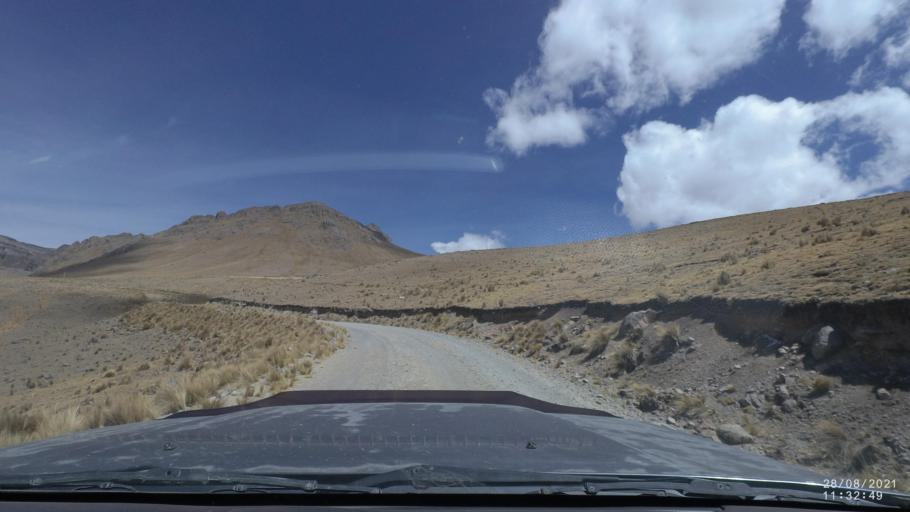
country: BO
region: Cochabamba
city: Sipe Sipe
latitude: -17.1834
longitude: -66.3682
